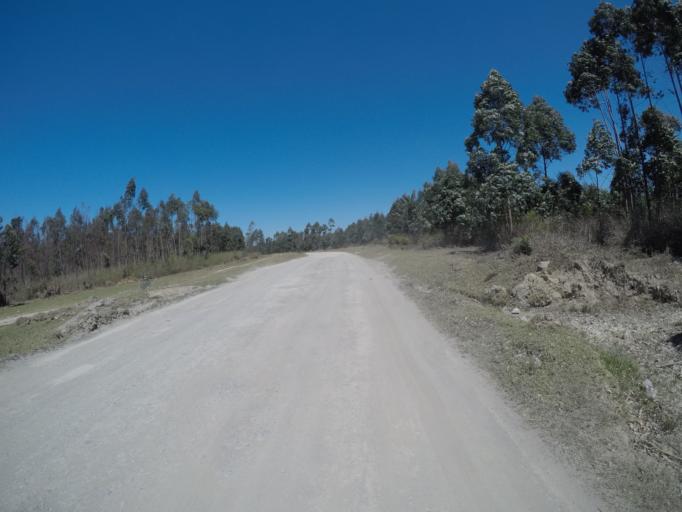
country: ZA
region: Eastern Cape
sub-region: OR Tambo District Municipality
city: Libode
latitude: -31.9525
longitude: 29.0236
